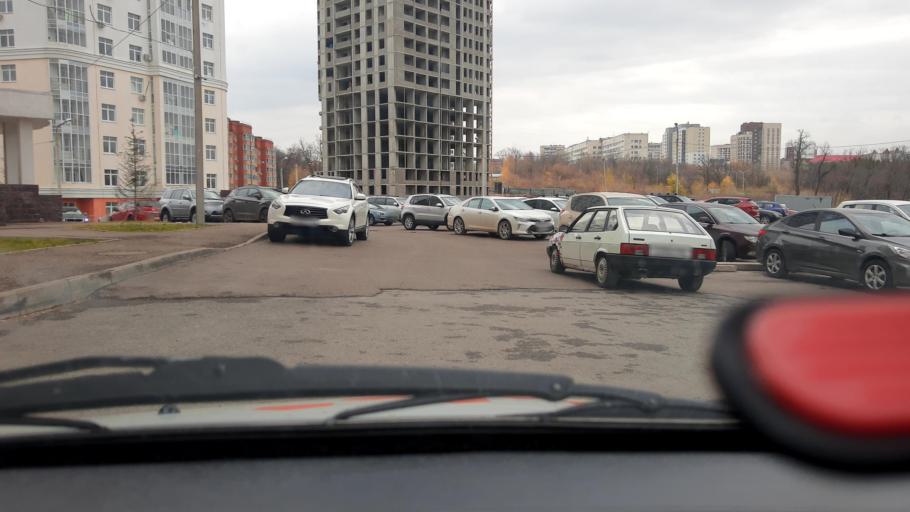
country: RU
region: Bashkortostan
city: Ufa
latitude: 54.7824
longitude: 56.0130
